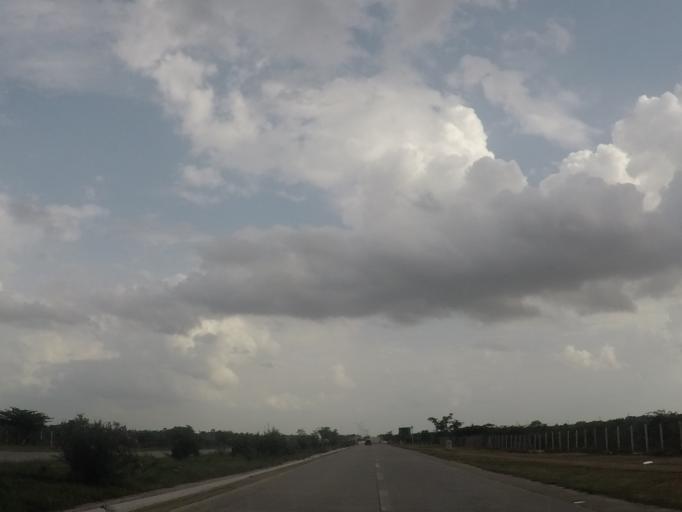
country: MM
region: Mandalay
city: Meiktila
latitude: 20.8293
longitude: 95.7676
